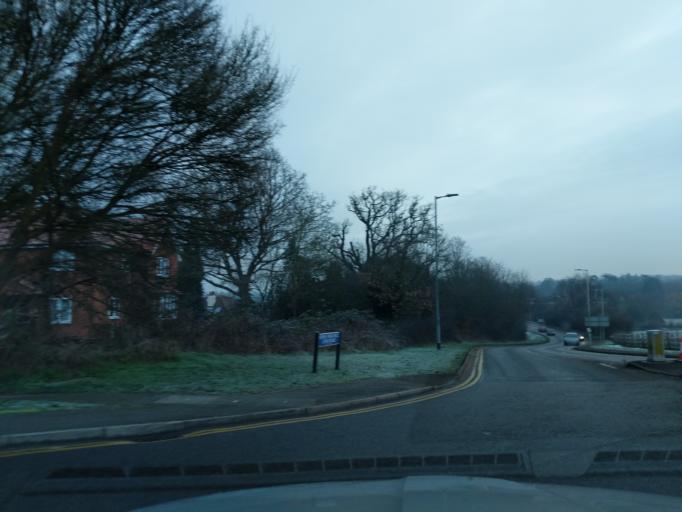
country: GB
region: England
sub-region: Hertfordshire
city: Kings Langley
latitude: 51.7062
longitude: -0.4458
